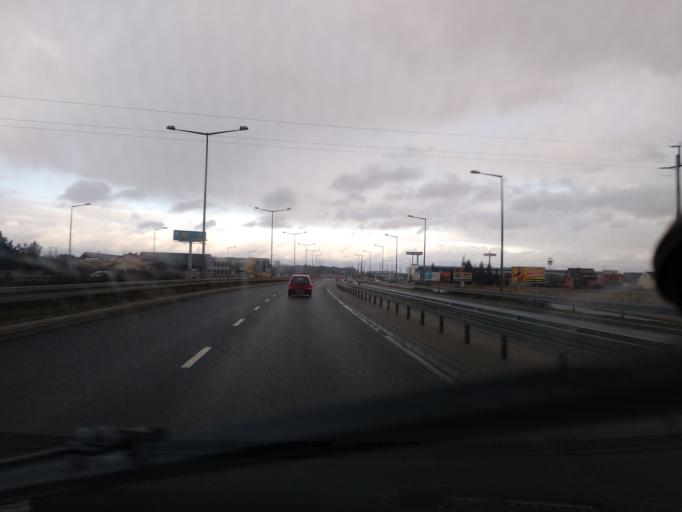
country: PL
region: Greater Poland Voivodeship
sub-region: Powiat koninski
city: Stare Miasto
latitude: 52.1823
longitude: 18.2247
